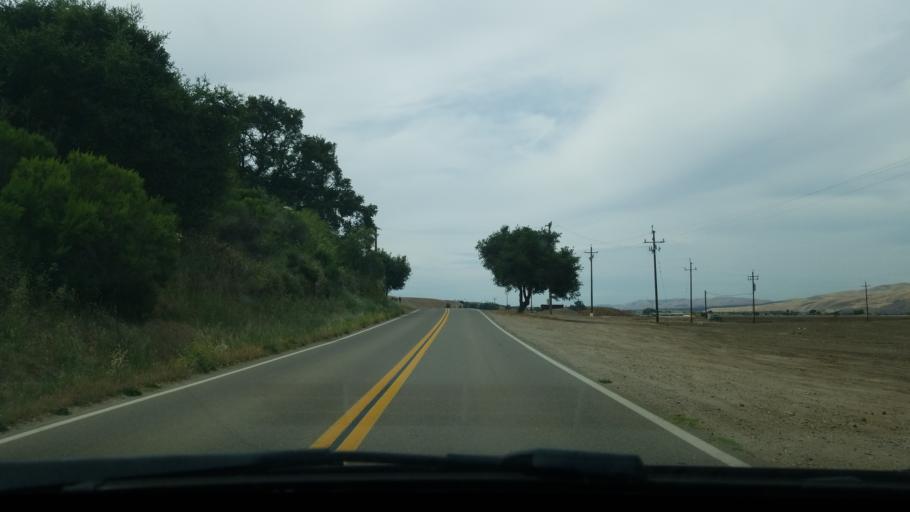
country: US
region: California
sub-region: Santa Barbara County
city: Los Alamos
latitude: 34.8716
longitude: -120.3030
